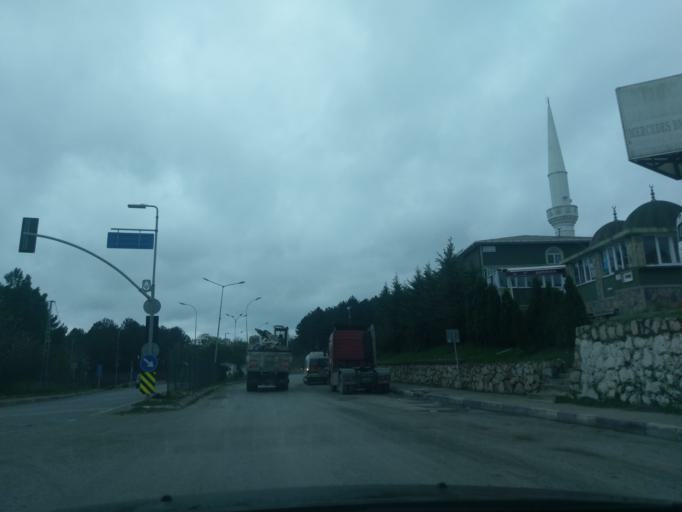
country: TR
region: Istanbul
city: Catalca
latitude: 41.1475
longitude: 28.4626
